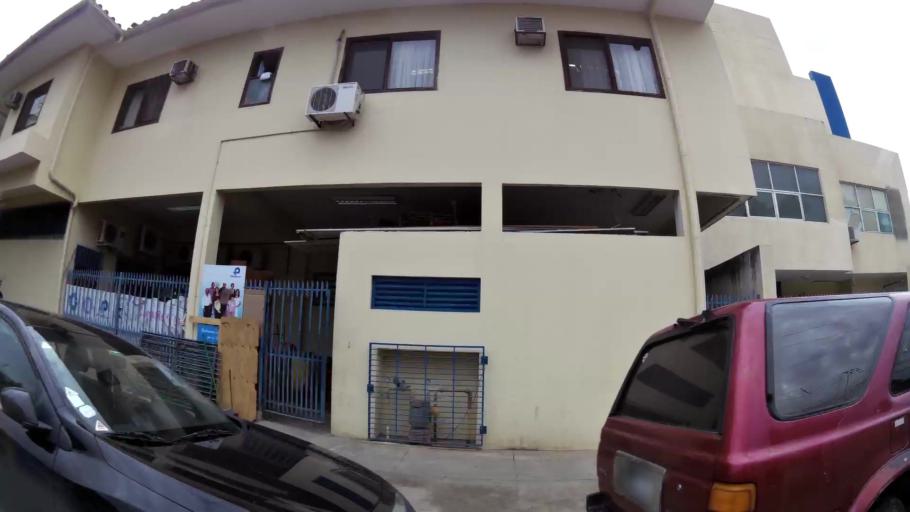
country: BO
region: Santa Cruz
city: Santa Cruz de la Sierra
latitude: -17.7666
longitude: -63.1703
